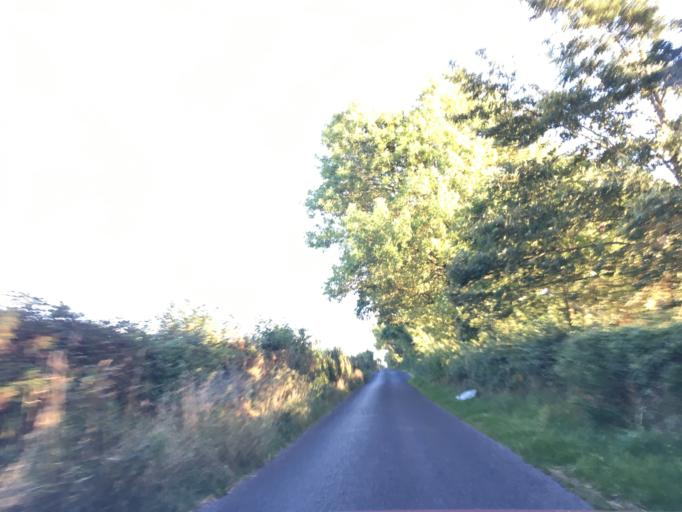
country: IE
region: Munster
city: Cashel
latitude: 52.5063
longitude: -7.9331
